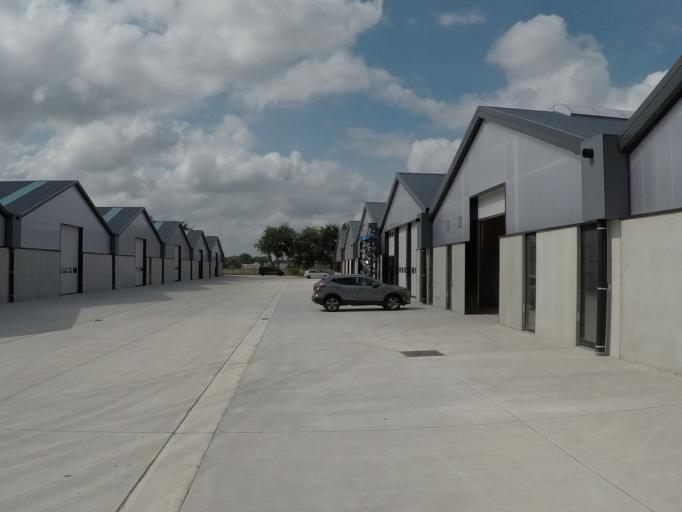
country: BE
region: Flanders
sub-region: Provincie Antwerpen
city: Ranst
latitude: 51.1741
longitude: 4.5773
